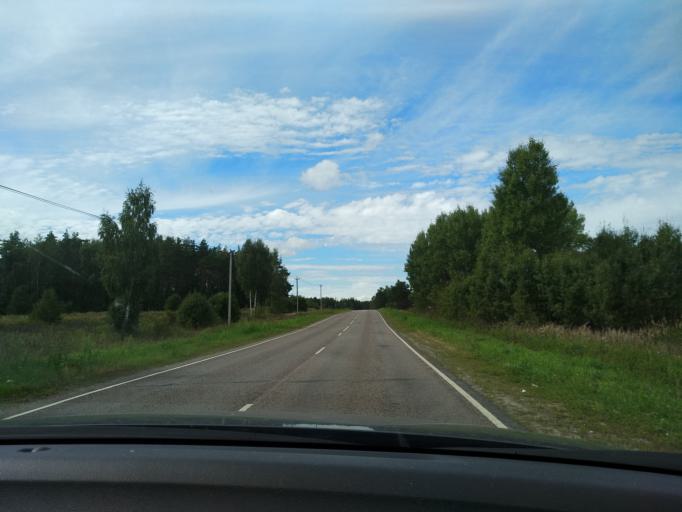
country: RU
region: Moskovskaya
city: Krasnyy Tkach
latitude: 55.3938
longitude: 39.1398
